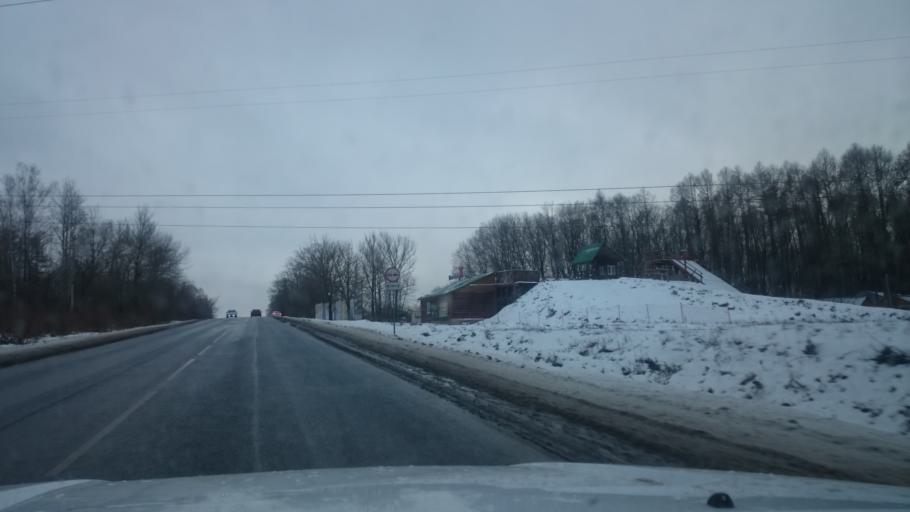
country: RU
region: Tula
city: Mendeleyevskiy
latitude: 54.1234
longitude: 37.5727
